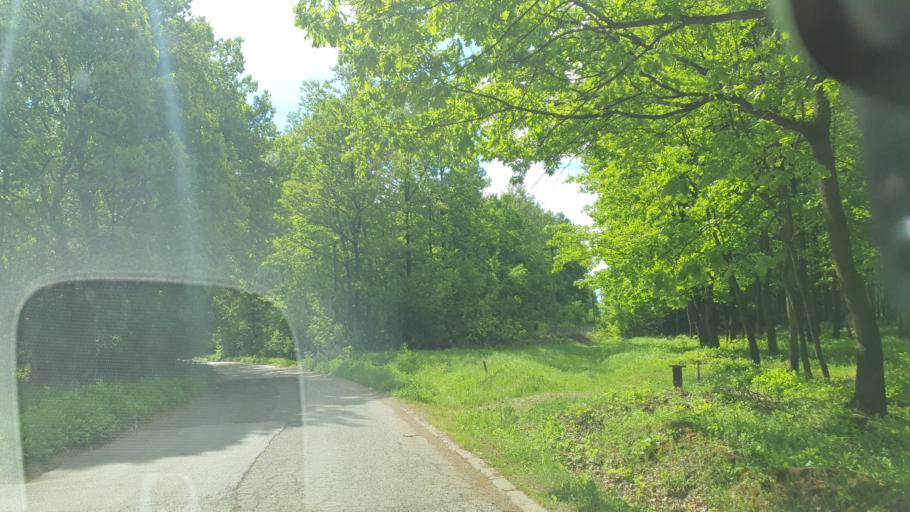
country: RS
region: Central Serbia
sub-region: Pomoravski Okrug
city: Cuprija
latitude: 43.9502
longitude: 21.4872
